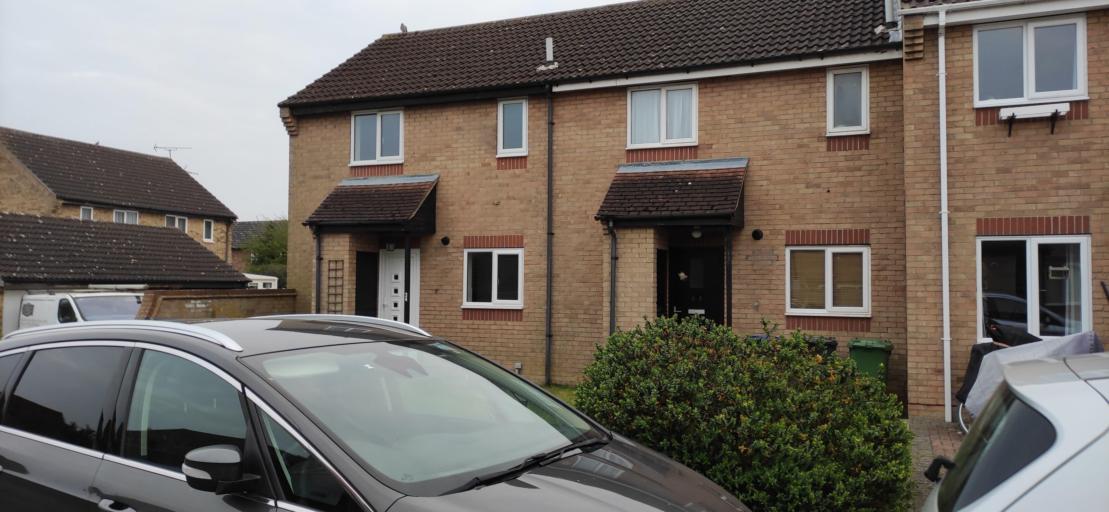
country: GB
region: England
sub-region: Cambridgeshire
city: Swavesey
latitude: 52.2499
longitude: 0.0170
